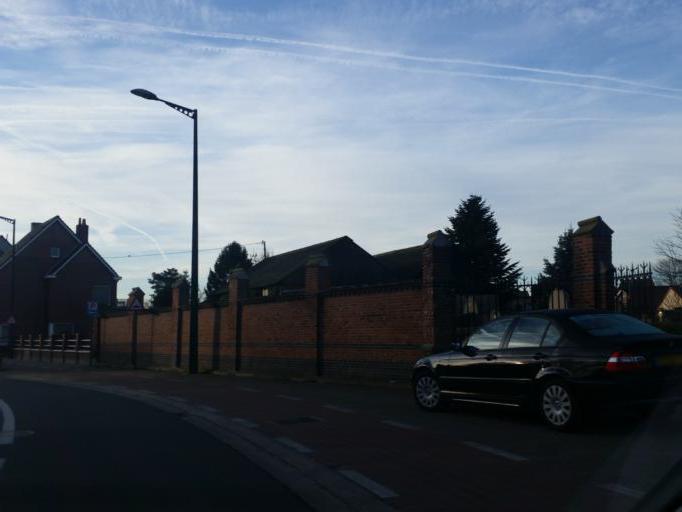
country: BE
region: Flanders
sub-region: Provincie Oost-Vlaanderen
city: Assenede
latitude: 51.1819
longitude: 3.7470
